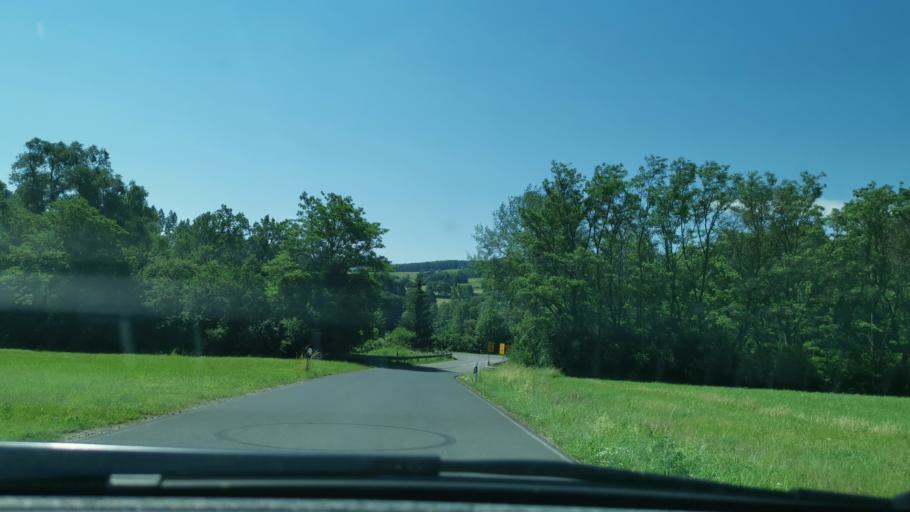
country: DE
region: Hesse
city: Spangenberg
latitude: 51.1139
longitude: 9.6998
